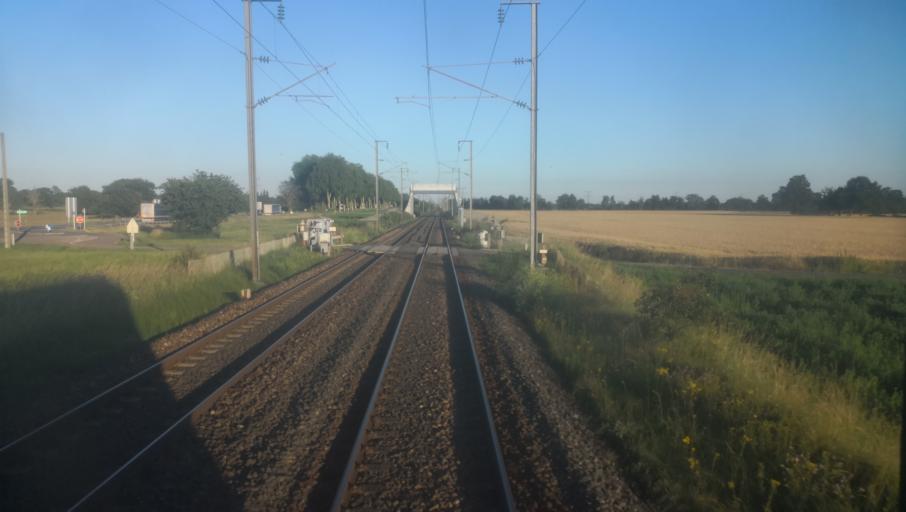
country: FR
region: Bourgogne
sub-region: Departement de la Nievre
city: Chantenay-Saint-Imbert
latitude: 46.7034
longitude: 3.2004
